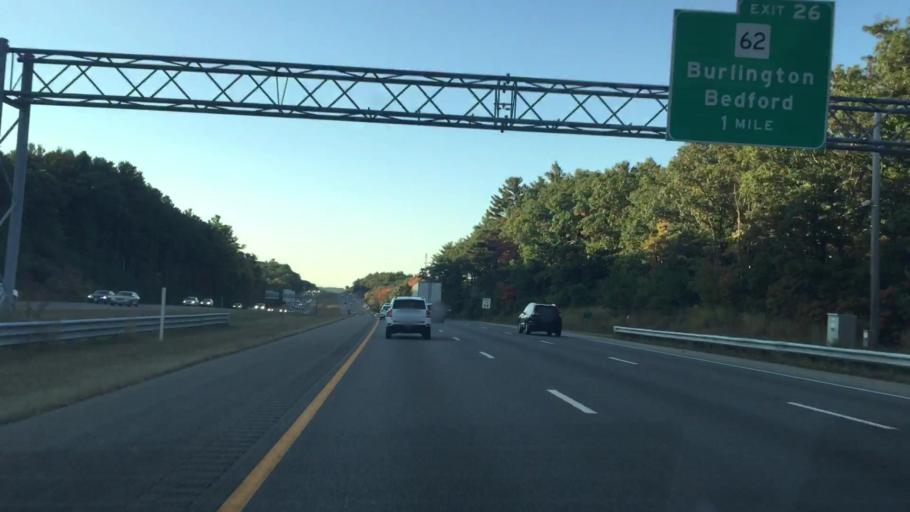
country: US
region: Massachusetts
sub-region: Middlesex County
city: Burlington
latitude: 42.4838
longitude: -71.2248
